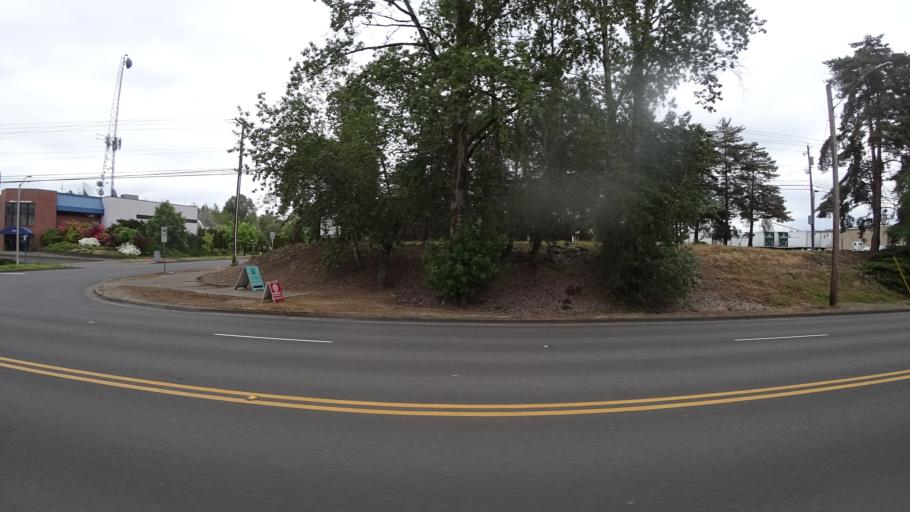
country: US
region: Oregon
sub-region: Washington County
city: Raleigh Hills
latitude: 45.4812
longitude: -122.7828
